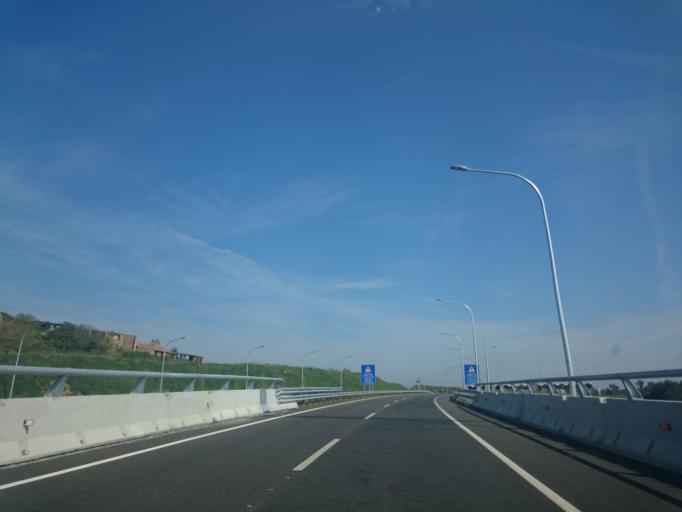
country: ES
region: Catalonia
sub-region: Provincia de Girona
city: Cervia de Ter
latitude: 42.0770
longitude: 2.8885
